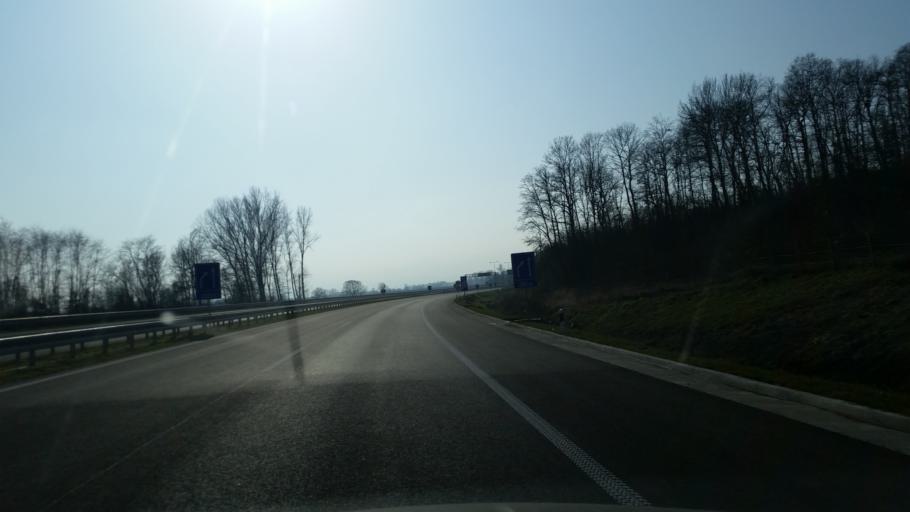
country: RS
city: Prislonica
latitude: 43.9282
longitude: 20.4016
